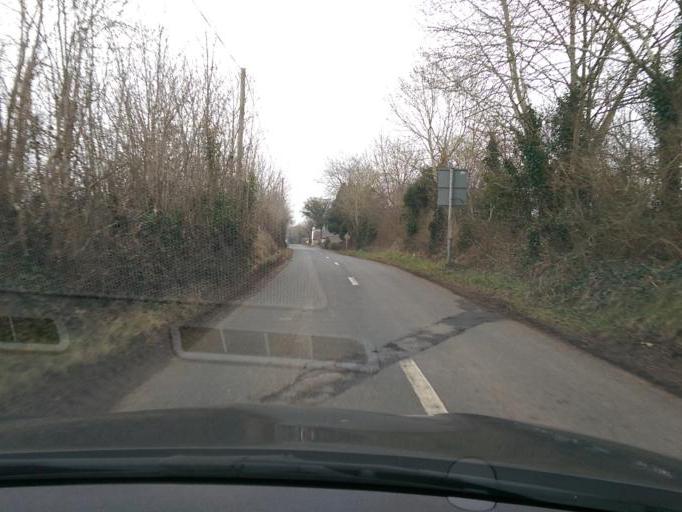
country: IE
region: Leinster
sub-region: An Longfort
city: Lanesborough
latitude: 53.6370
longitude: -7.8935
